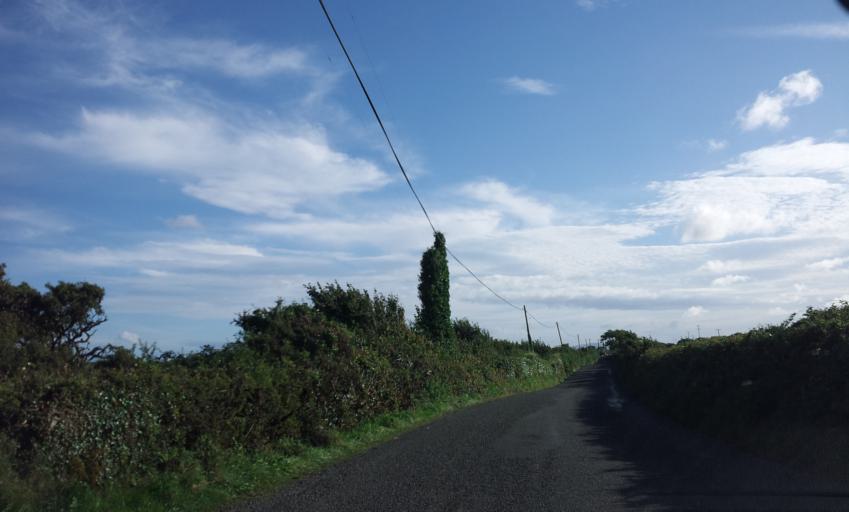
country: IE
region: Munster
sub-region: An Clar
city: Ennis
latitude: 52.9975
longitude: -9.1291
